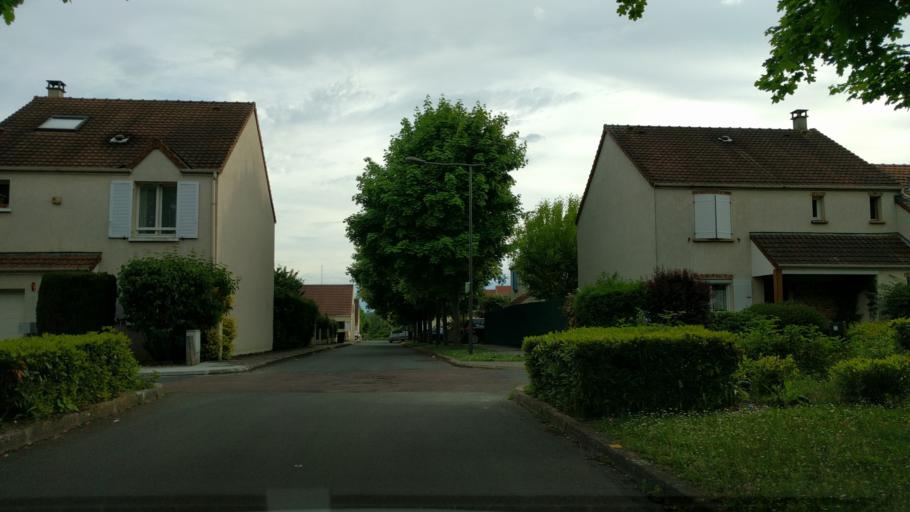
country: FR
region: Ile-de-France
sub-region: Departement de Seine-et-Marne
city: Savigny-le-Temple
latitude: 48.5729
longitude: 2.5892
